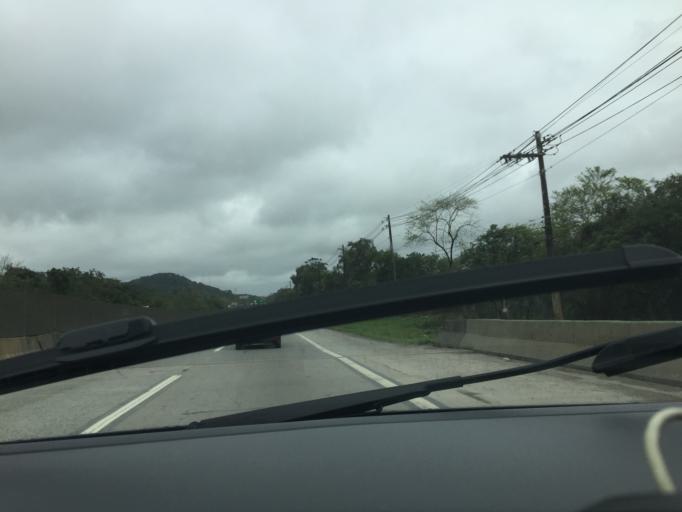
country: BR
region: Sao Paulo
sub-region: Santos
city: Santos
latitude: -23.9031
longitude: -46.2973
